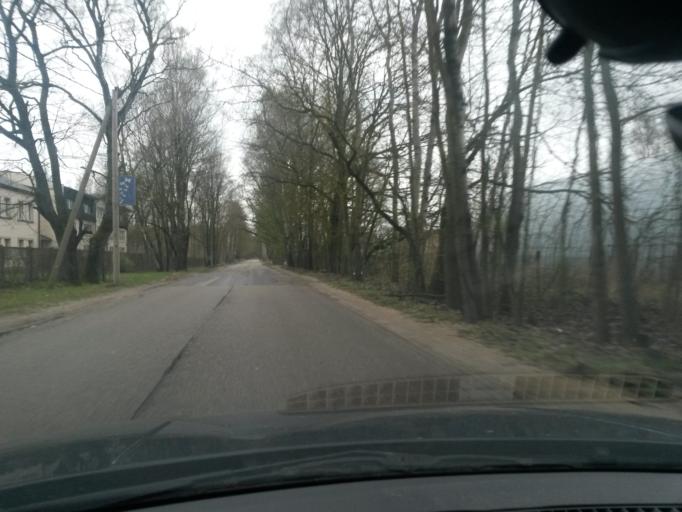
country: LV
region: Kekava
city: Kekava
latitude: 56.8947
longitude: 24.2377
